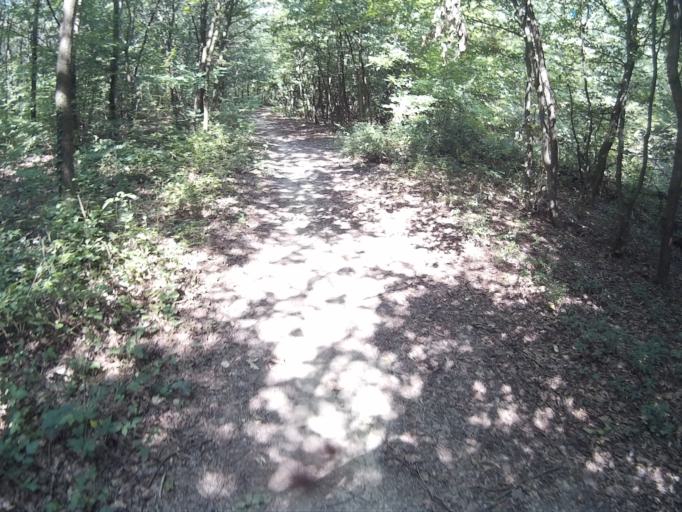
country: HU
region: Vas
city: Szombathely
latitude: 47.2190
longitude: 16.5548
